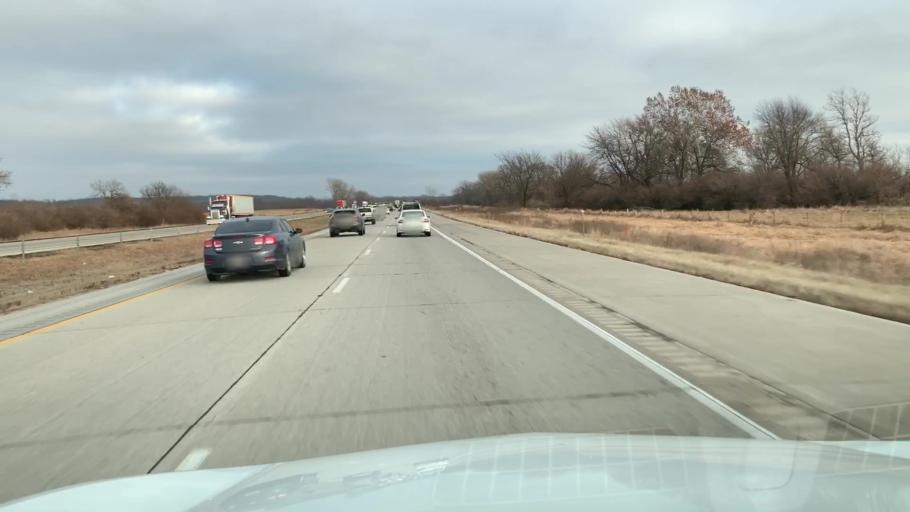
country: US
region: Iowa
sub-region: Polk County
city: Mitchellville
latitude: 41.6814
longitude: -93.3212
